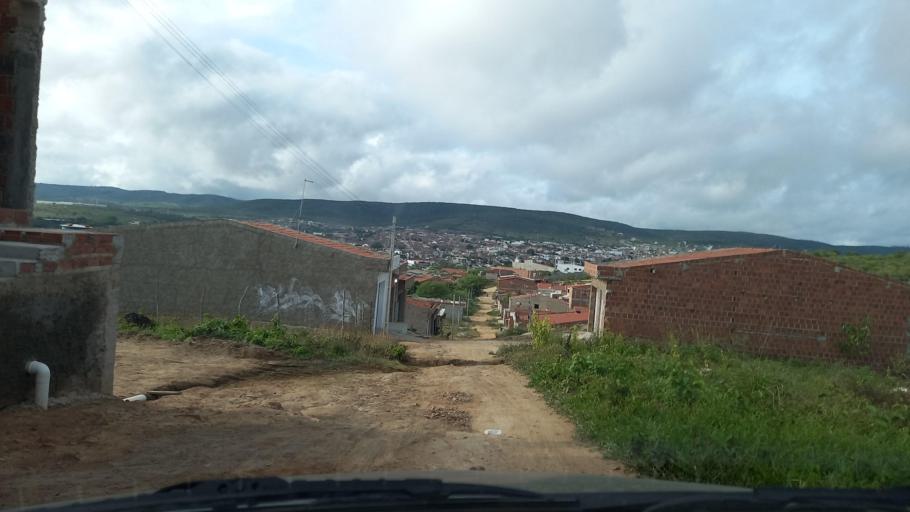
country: BR
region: Pernambuco
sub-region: Bezerros
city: Bezerros
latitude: -8.2217
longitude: -35.7553
